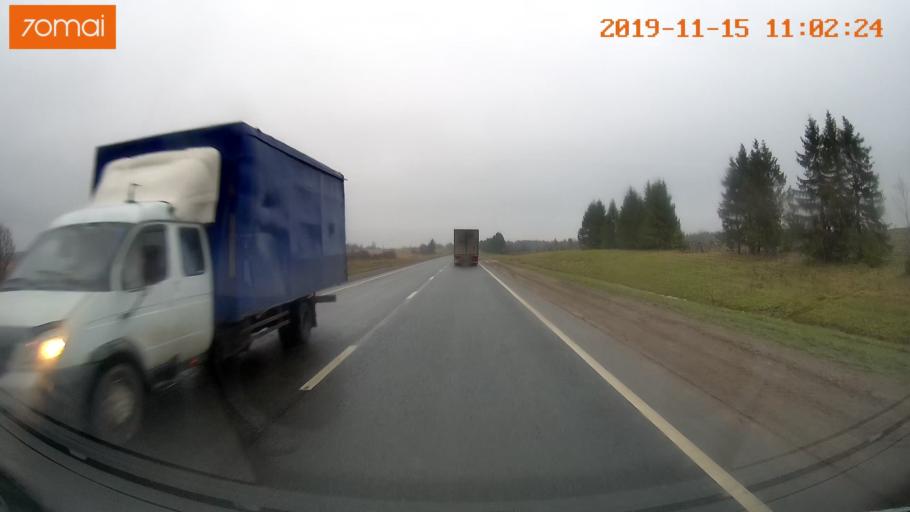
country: RU
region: Vologda
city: Chebsara
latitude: 59.1288
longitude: 38.9407
